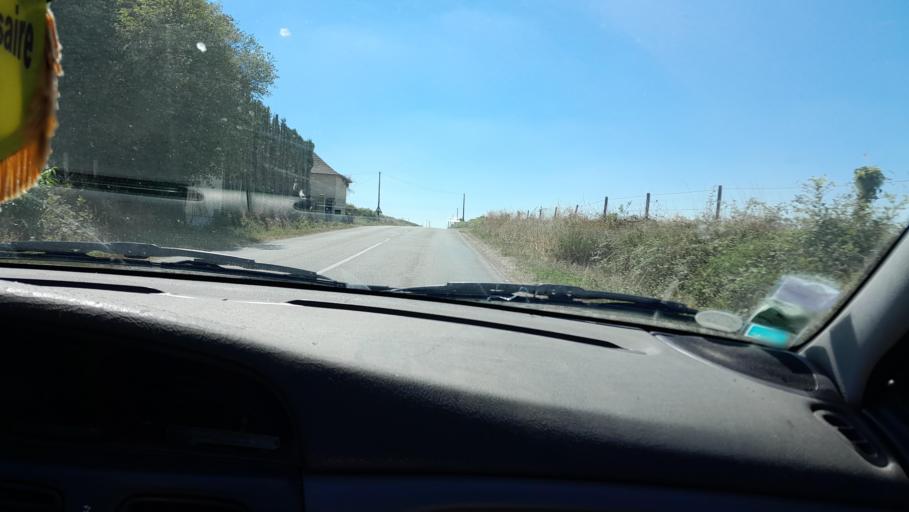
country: FR
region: Pays de la Loire
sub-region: Departement de la Mayenne
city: Ballots
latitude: 47.9551
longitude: -1.0597
